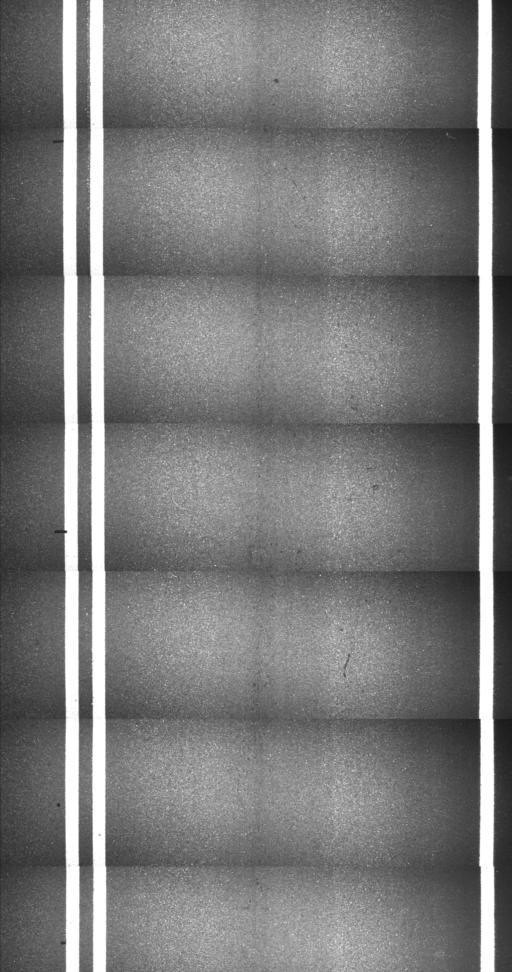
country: US
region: Vermont
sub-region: Orange County
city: Randolph
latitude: 43.9948
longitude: -72.7523
